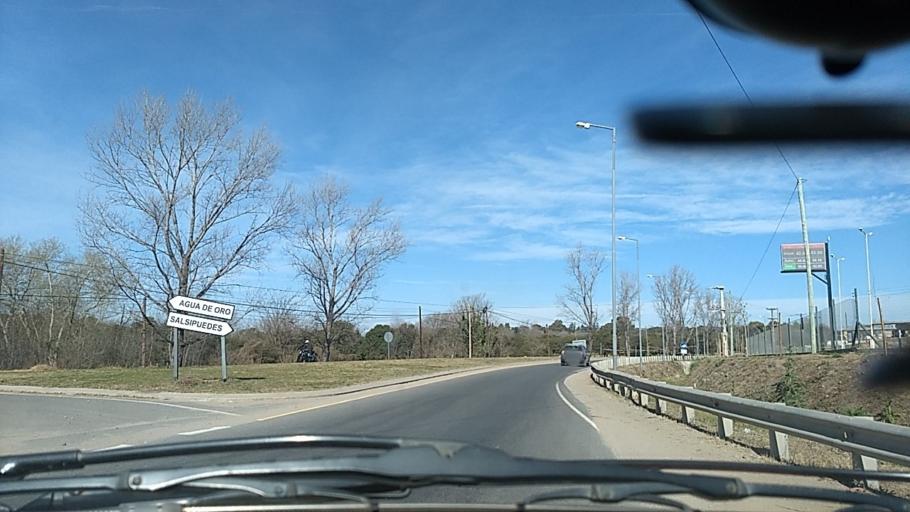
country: AR
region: Cordoba
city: Salsipuedes
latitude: -31.1265
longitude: -64.2947
